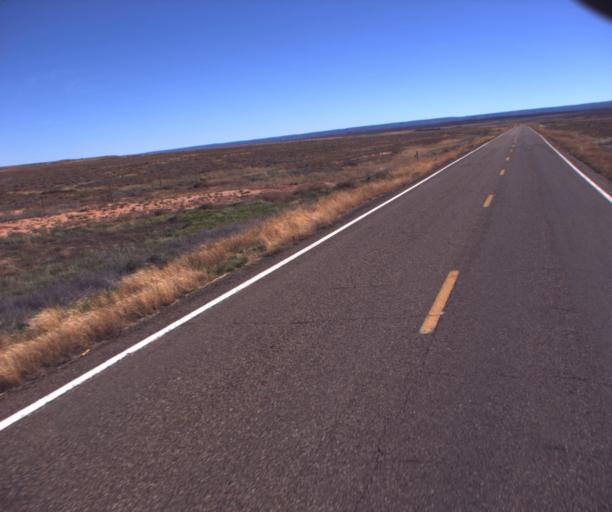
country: US
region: Arizona
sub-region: Coconino County
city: Fredonia
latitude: 36.9251
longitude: -112.4638
